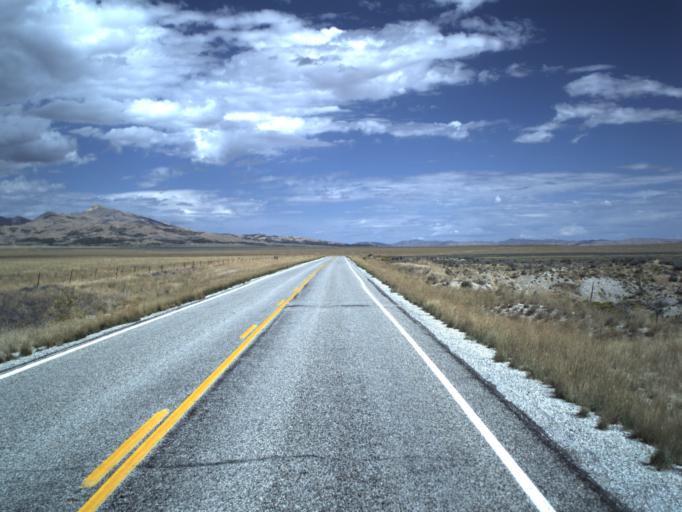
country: US
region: Idaho
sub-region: Oneida County
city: Malad City
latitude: 41.9375
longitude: -113.0858
